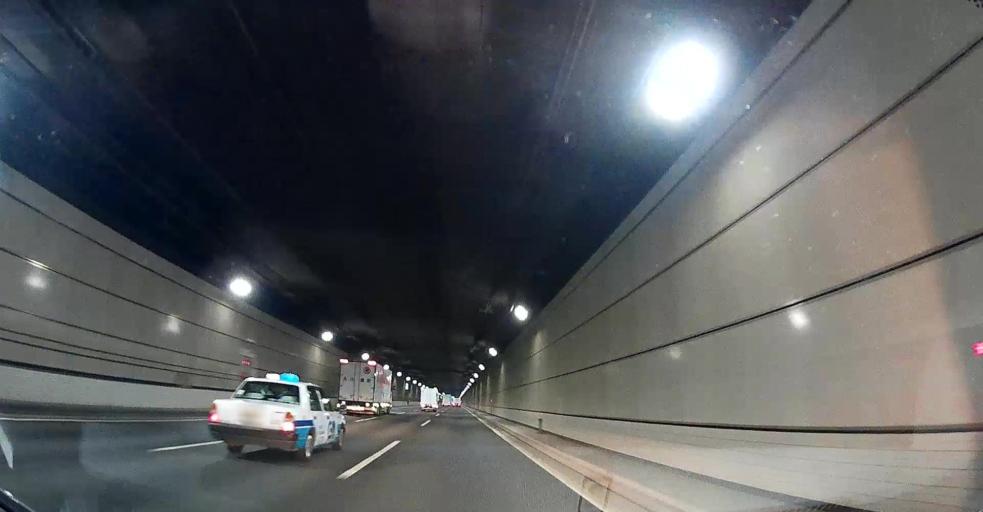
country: JP
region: Kanagawa
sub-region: Kawasaki-shi
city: Kawasaki
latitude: 35.5097
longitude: 139.7817
